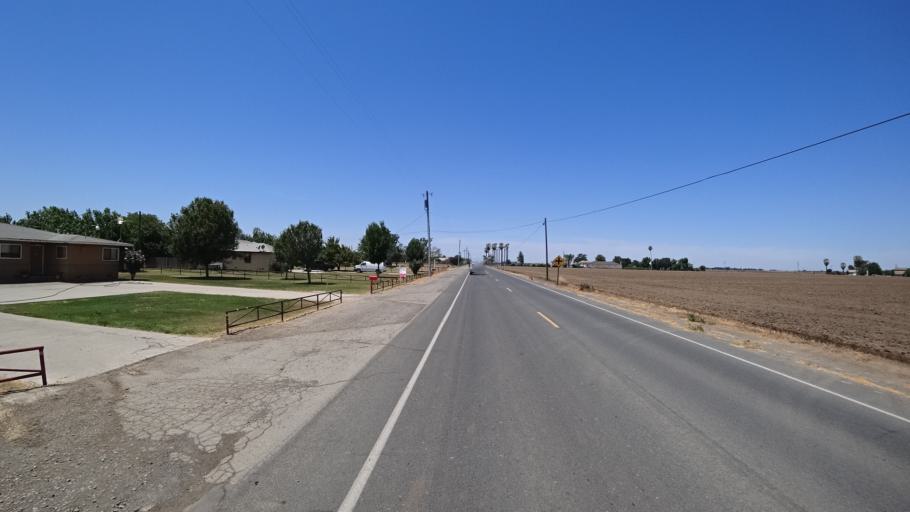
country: US
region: California
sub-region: Kings County
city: Armona
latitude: 36.3426
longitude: -119.7416
